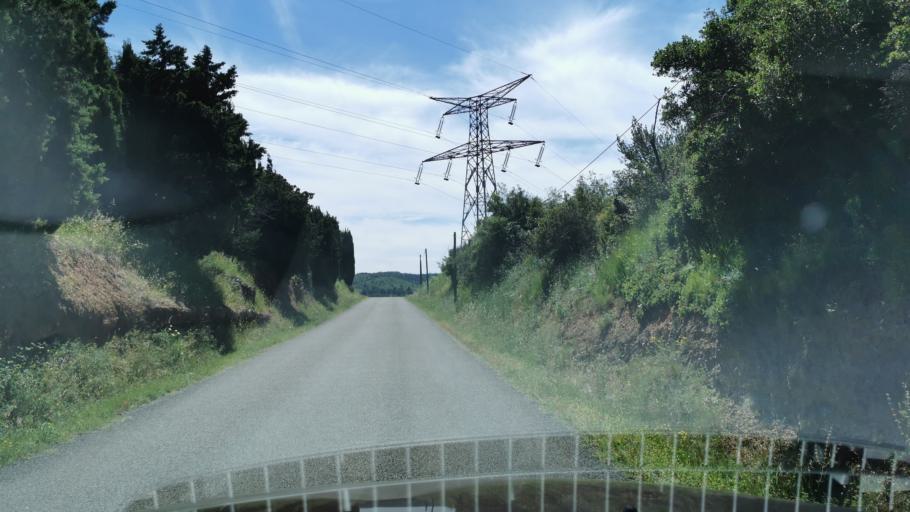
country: FR
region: Languedoc-Roussillon
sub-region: Departement de l'Aude
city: Nevian
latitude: 43.2011
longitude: 2.9021
